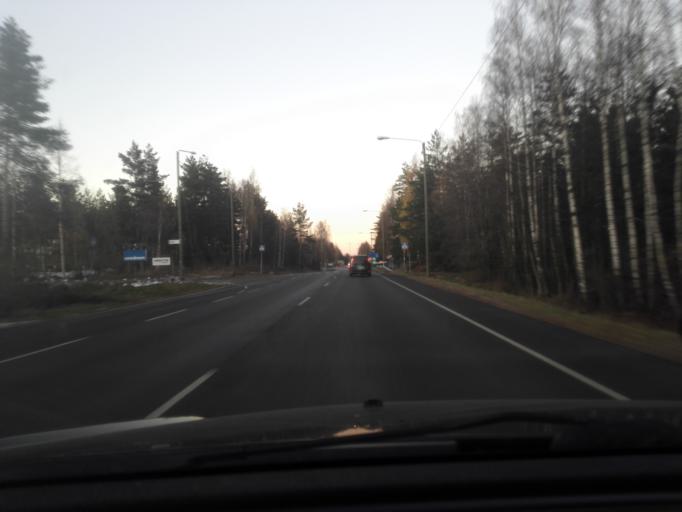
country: FI
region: Uusimaa
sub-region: Helsinki
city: Vantaa
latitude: 60.3018
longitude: 25.1039
